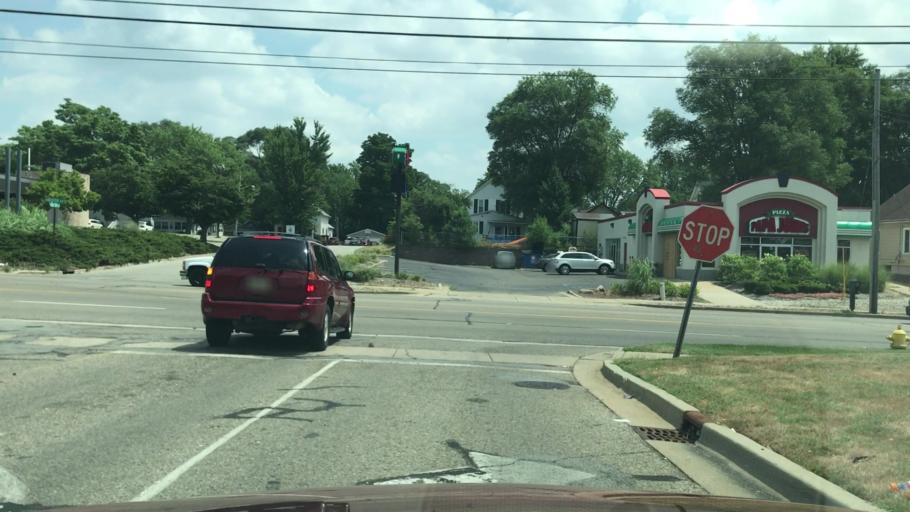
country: US
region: Michigan
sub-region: Kent County
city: Comstock Park
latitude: 43.0086
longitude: -85.6890
